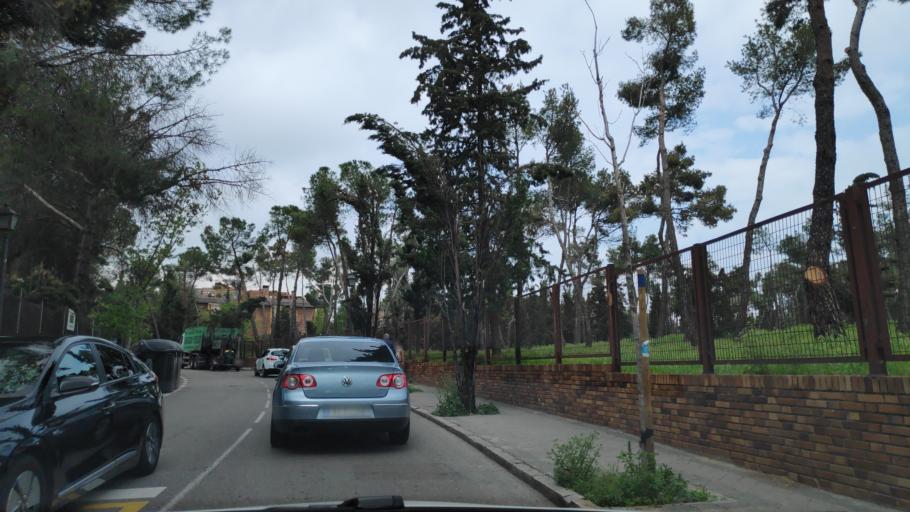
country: ES
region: Madrid
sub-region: Provincia de Madrid
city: Pozuelo de Alarcon
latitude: 40.4608
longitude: -3.7802
